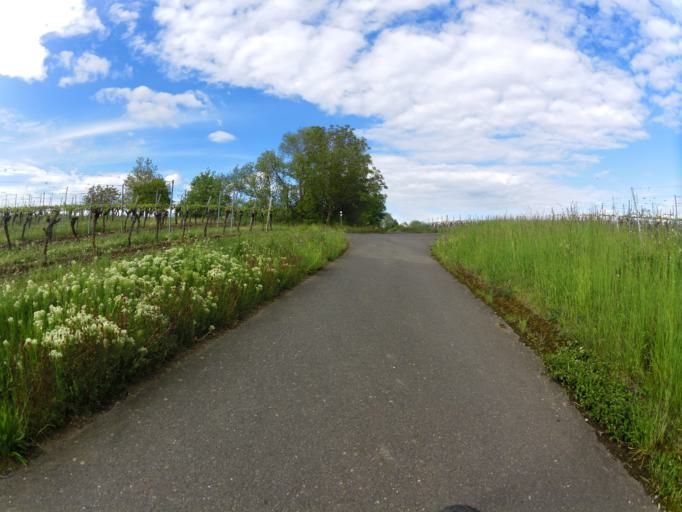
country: DE
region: Bavaria
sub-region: Regierungsbezirk Unterfranken
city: Nordheim
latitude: 49.8429
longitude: 10.1858
